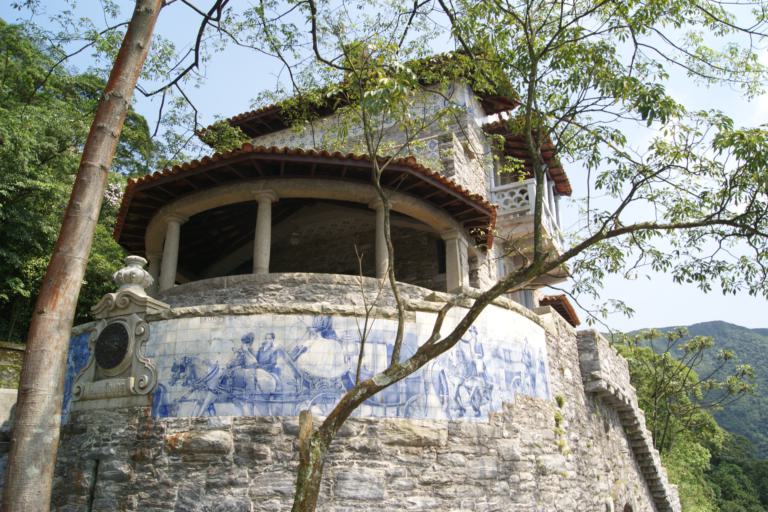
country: BR
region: Sao Paulo
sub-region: Cubatao
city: Cubatao
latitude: -23.8635
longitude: -46.4529
